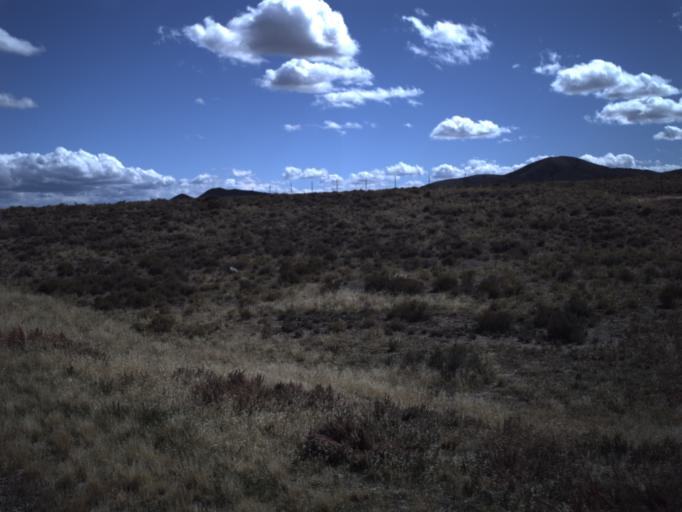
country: US
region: Utah
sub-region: Beaver County
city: Milford
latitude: 38.4337
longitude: -113.1341
